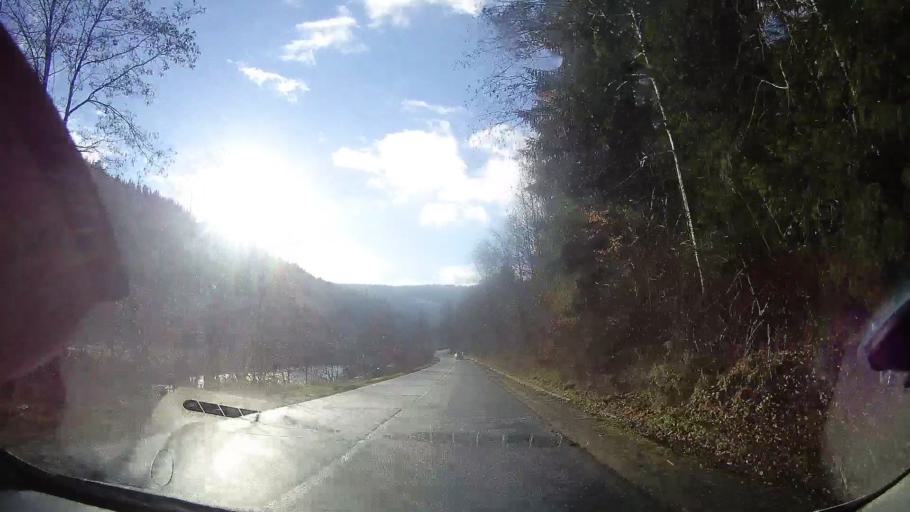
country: RO
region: Alba
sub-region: Comuna Vadu Motilor
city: Vadu Motilor
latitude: 46.4085
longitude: 22.9641
